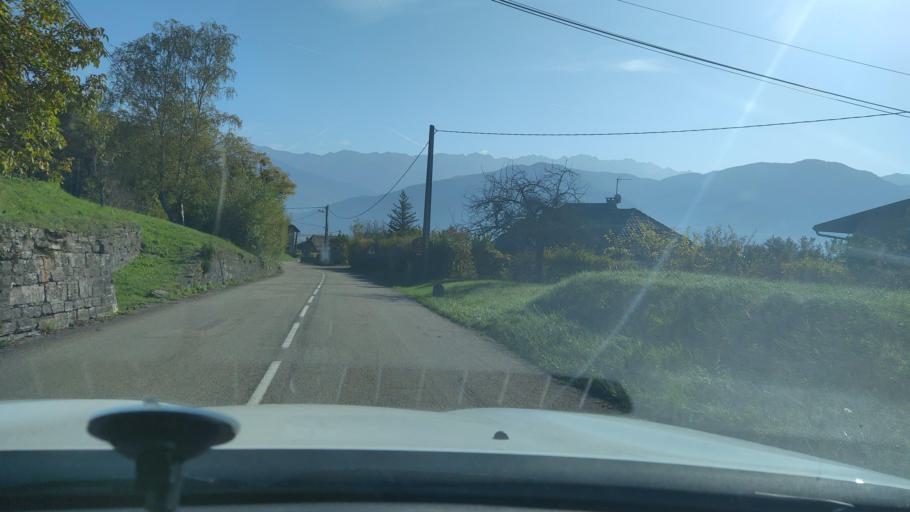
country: FR
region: Rhone-Alpes
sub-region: Departement de la Savoie
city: Coise-Saint-Jean-Pied-Gauthier
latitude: 45.5742
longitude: 6.1577
